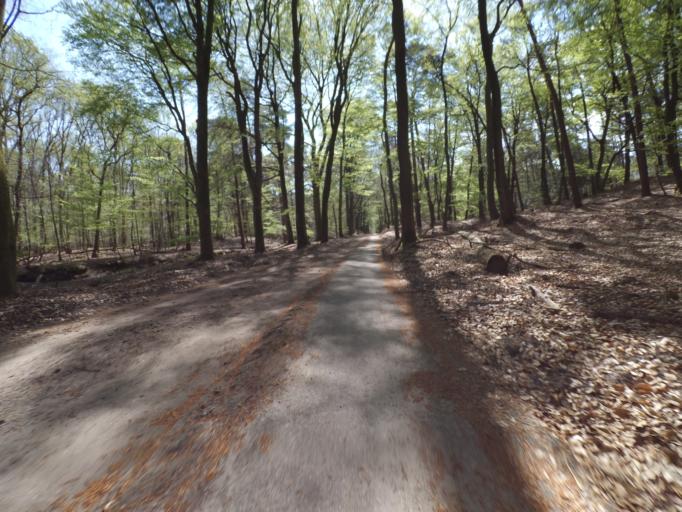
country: NL
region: Gelderland
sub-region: Gemeente Ermelo
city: Ermelo
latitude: 52.3198
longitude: 5.7045
